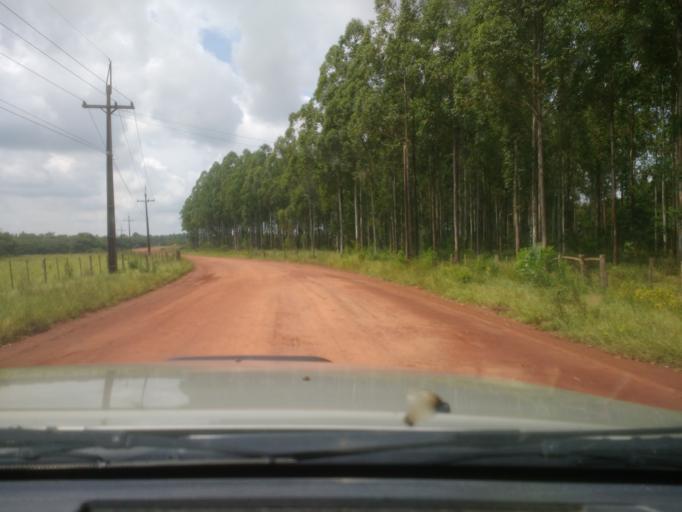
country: PY
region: San Pedro
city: Puerto Rosario
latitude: -24.4034
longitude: -57.1041
